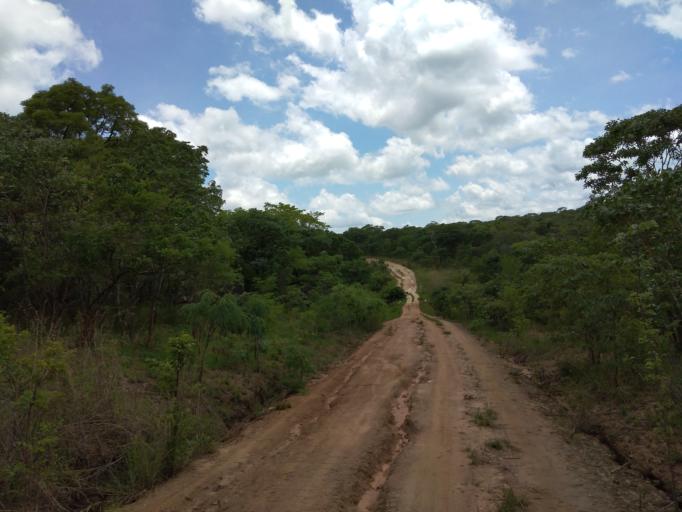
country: ZM
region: Central
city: Mkushi
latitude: -13.9987
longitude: 29.9531
